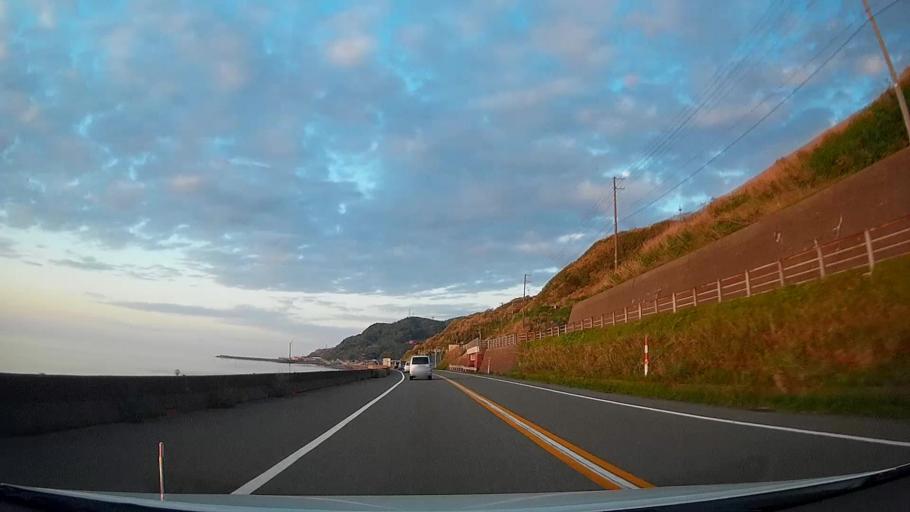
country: JP
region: Niigata
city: Joetsu
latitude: 37.1516
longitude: 138.0736
